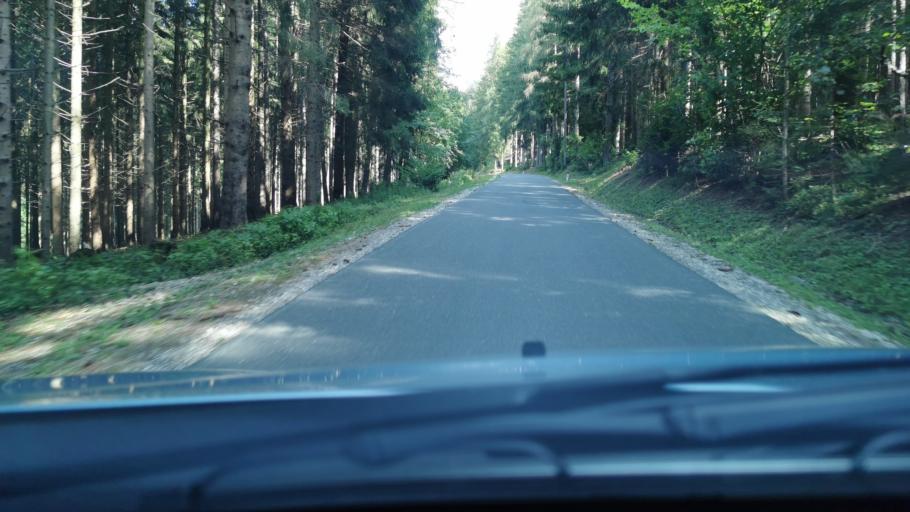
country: AT
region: Styria
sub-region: Politischer Bezirk Weiz
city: Baierdorf-Umgebung
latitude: 47.3059
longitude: 15.7061
